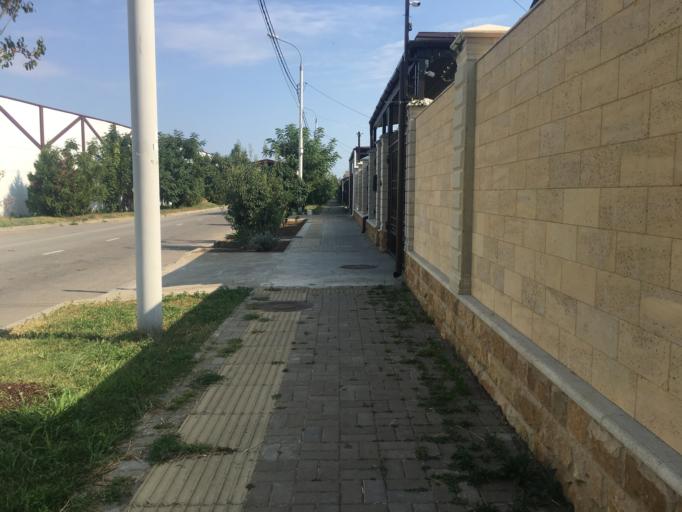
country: RU
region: Krasnodarskiy
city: Vysokoye
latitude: 43.3960
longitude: 39.9998
